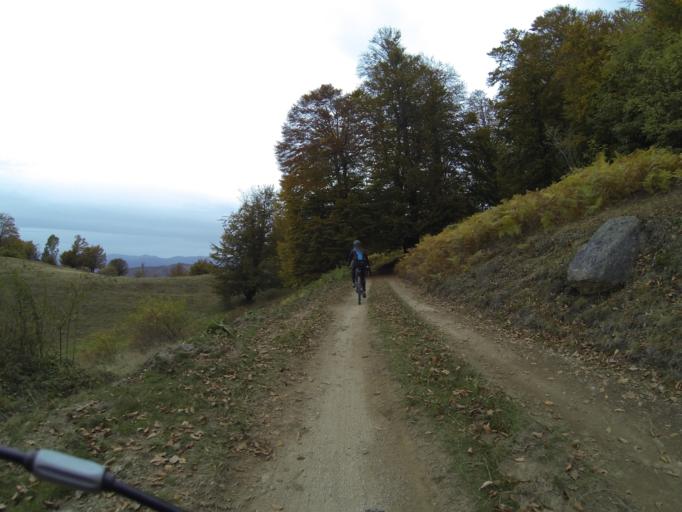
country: RO
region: Gorj
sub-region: Comuna Tismana
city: Sohodol
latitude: 45.1274
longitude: 22.8631
